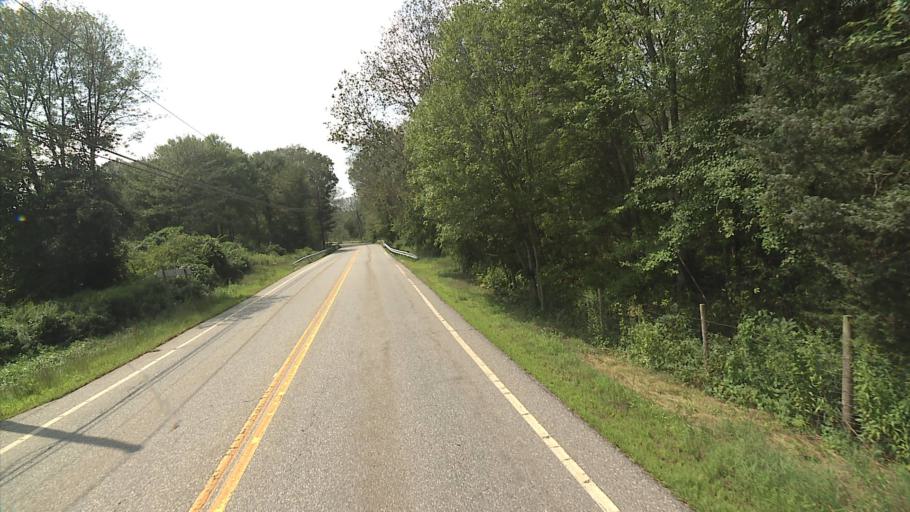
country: US
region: Connecticut
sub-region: Middlesex County
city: Essex Village
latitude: 41.4420
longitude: -72.3317
